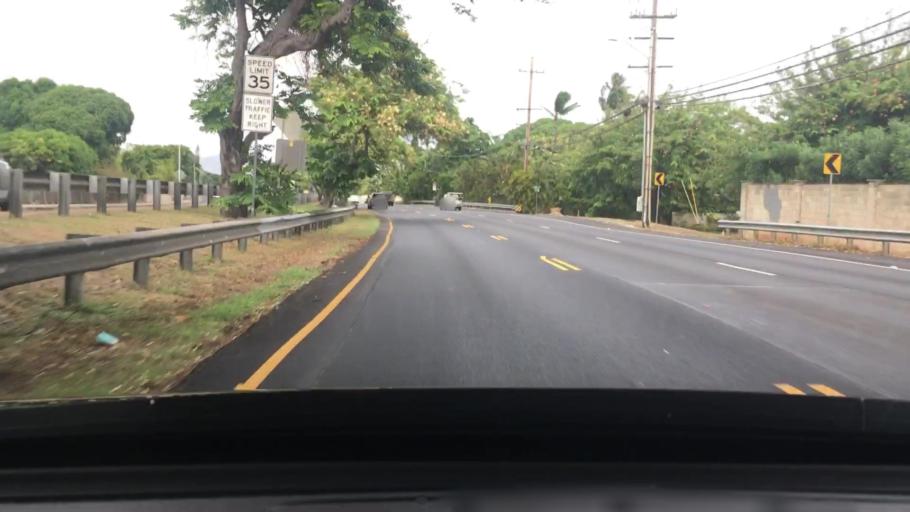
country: US
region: Hawaii
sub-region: Honolulu County
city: Waimanalo
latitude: 21.2759
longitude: -157.7667
